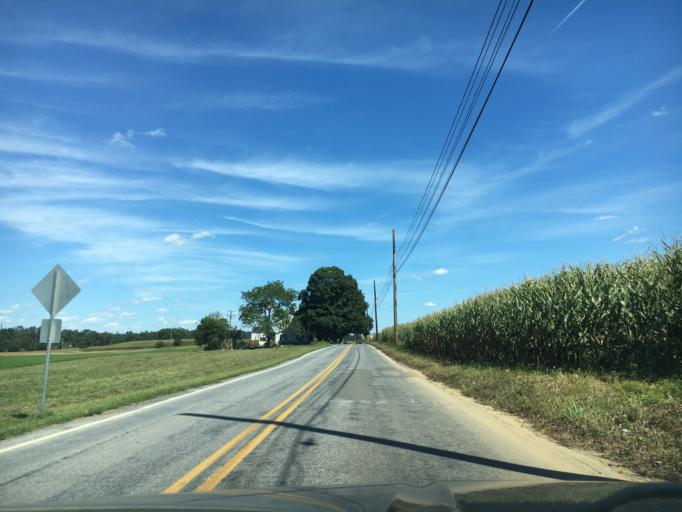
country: US
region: Pennsylvania
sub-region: Berks County
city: Topton
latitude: 40.5279
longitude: -75.6844
